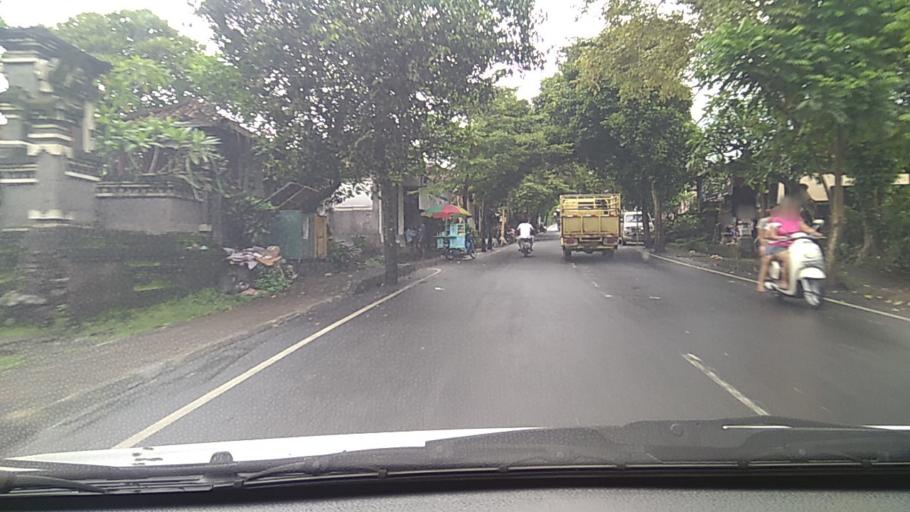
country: ID
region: Bali
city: Banjar Budakeling
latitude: -8.4362
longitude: 115.5905
